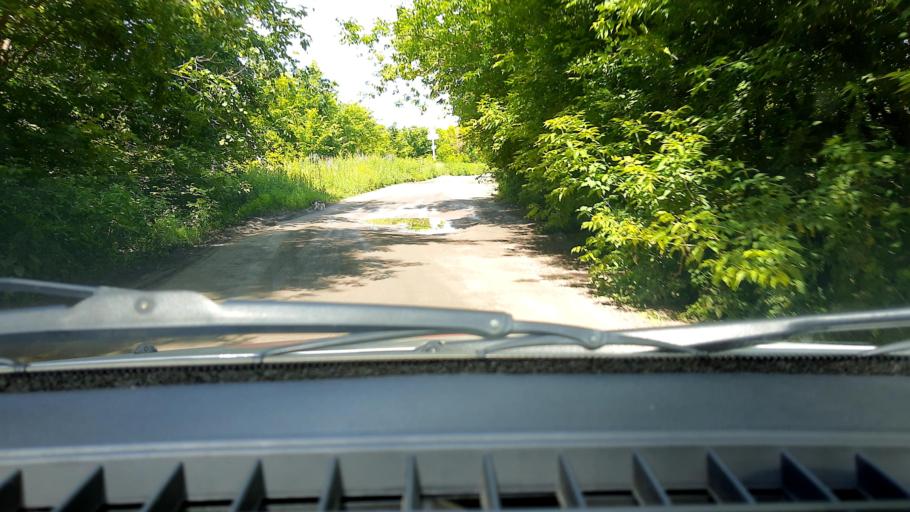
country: RU
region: Bashkortostan
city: Ufa
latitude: 54.6911
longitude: 56.0531
